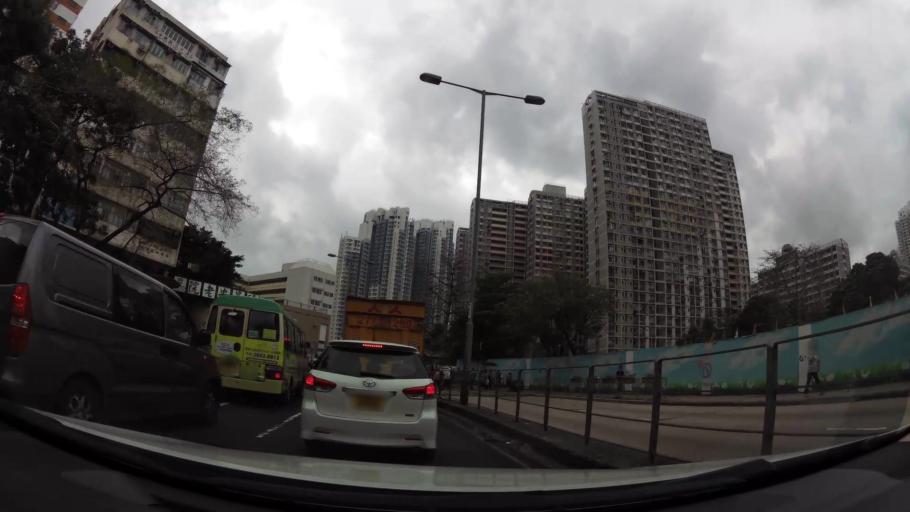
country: HK
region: Wong Tai Sin
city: Wong Tai Sin
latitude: 22.3351
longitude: 114.1942
